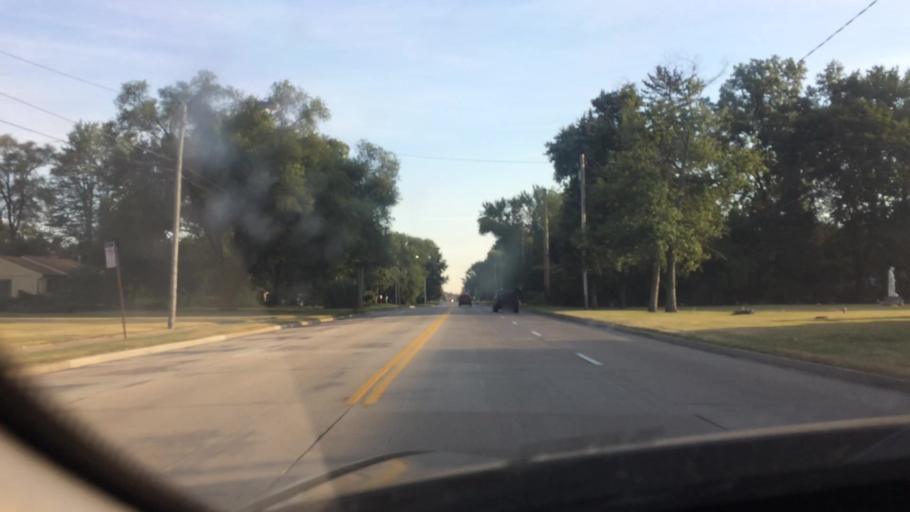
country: US
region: Ohio
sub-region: Lucas County
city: Ottawa Hills
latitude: 41.6821
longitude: -83.6442
